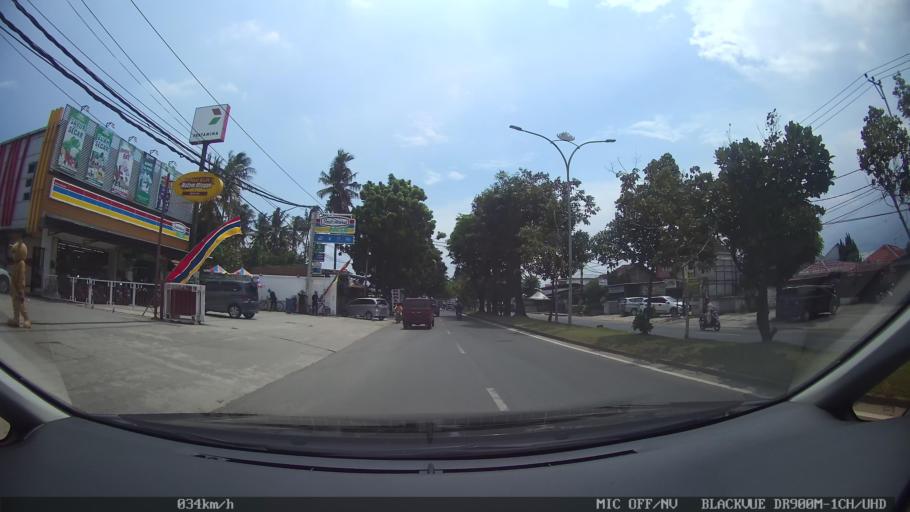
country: ID
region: Lampung
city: Kedaton
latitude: -5.3811
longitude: 105.2697
